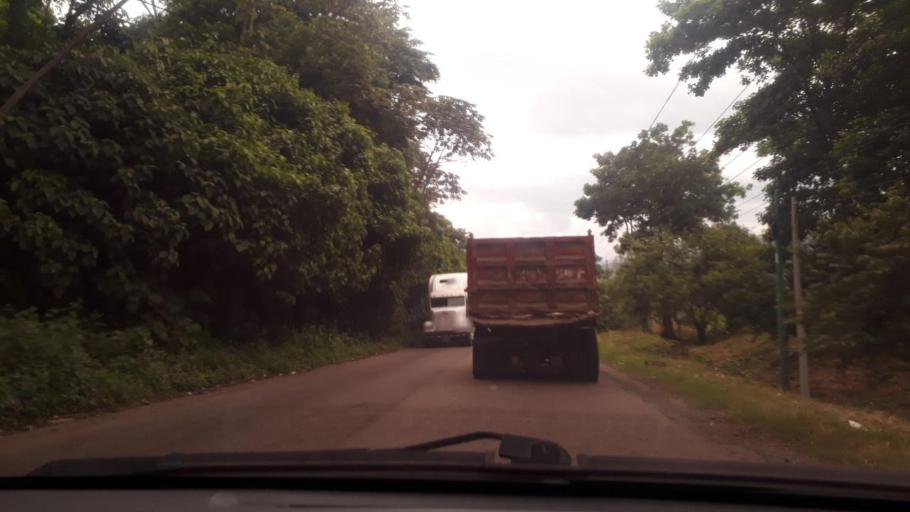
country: GT
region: Santa Rosa
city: Cuilapa
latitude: 14.2543
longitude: -90.2412
